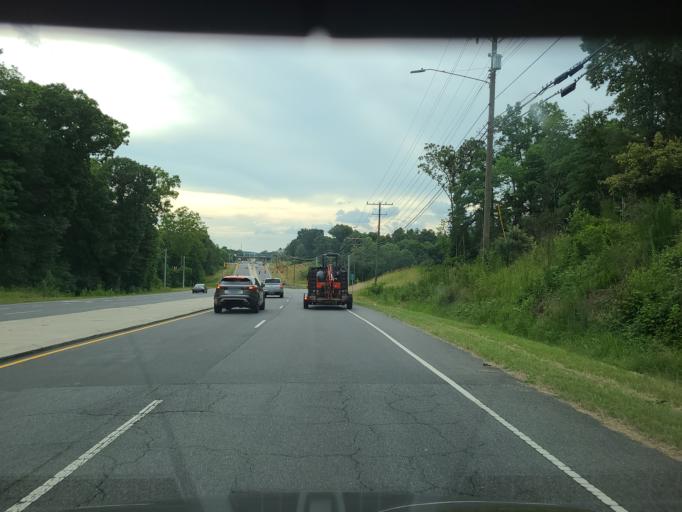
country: US
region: North Carolina
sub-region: Gaston County
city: Belmont
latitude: 35.2381
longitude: -80.9606
